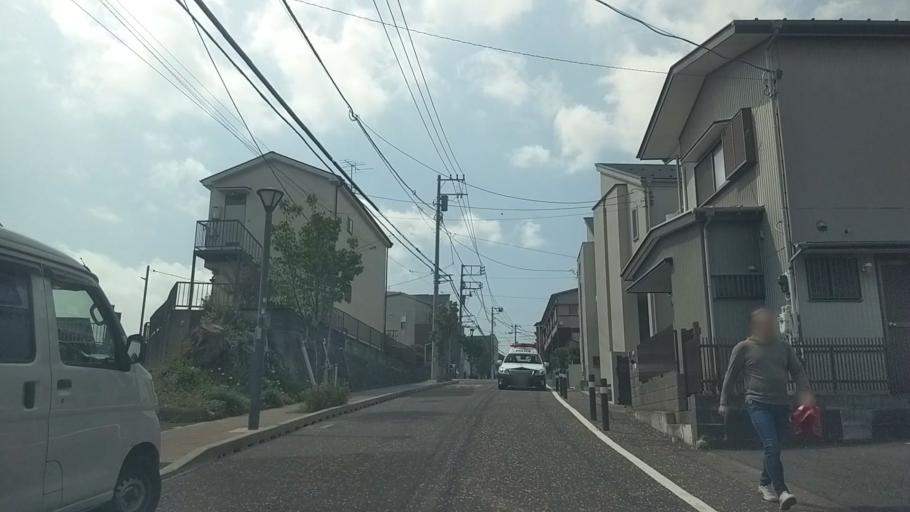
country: JP
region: Kanagawa
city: Yokohama
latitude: 35.3951
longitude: 139.5921
